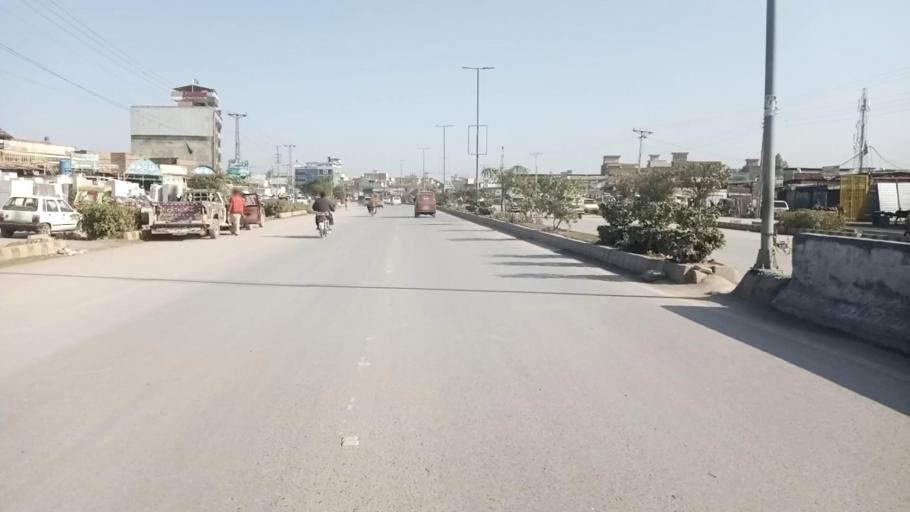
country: PK
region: Khyber Pakhtunkhwa
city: Peshawar
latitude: 34.0311
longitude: 71.5918
